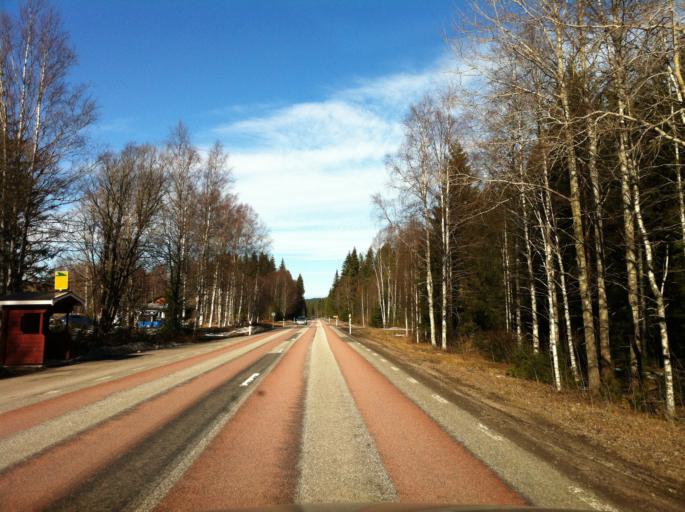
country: SE
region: Vaermland
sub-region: Filipstads Kommun
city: Filipstad
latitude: 59.7389
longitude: 14.2284
